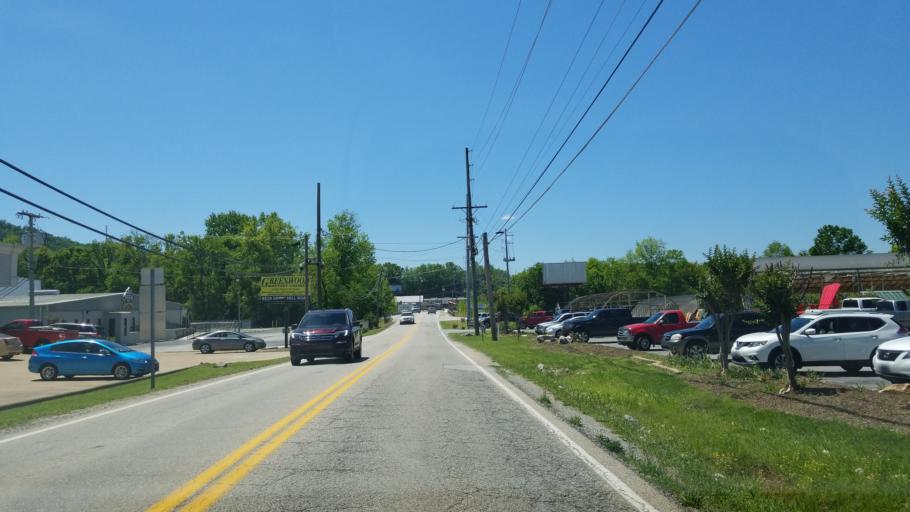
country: US
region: Tennessee
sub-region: Hamilton County
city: Collegedale
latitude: 35.0803
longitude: -85.0594
